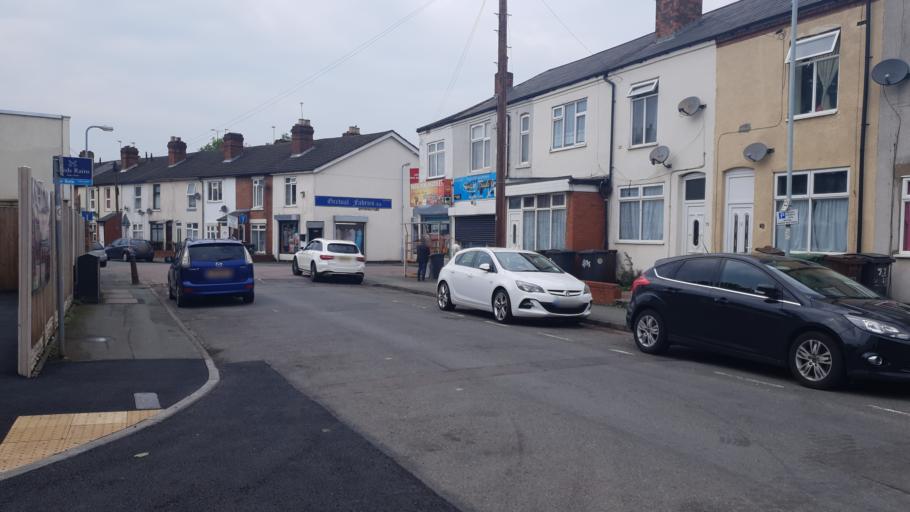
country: GB
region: England
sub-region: Wolverhampton
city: Wolverhampton
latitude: 52.5944
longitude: -2.1363
